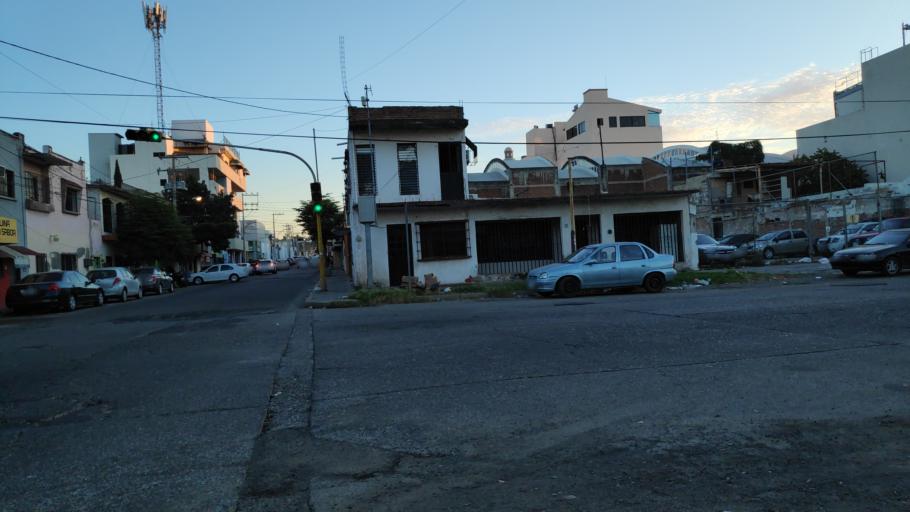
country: MX
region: Sinaloa
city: Culiacan
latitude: 24.7984
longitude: -107.3927
